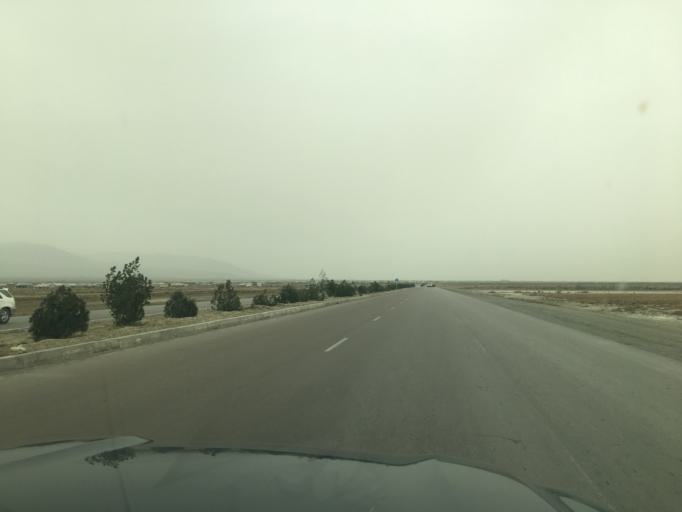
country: TM
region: Ahal
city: Baharly
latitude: 38.3739
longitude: 57.5124
